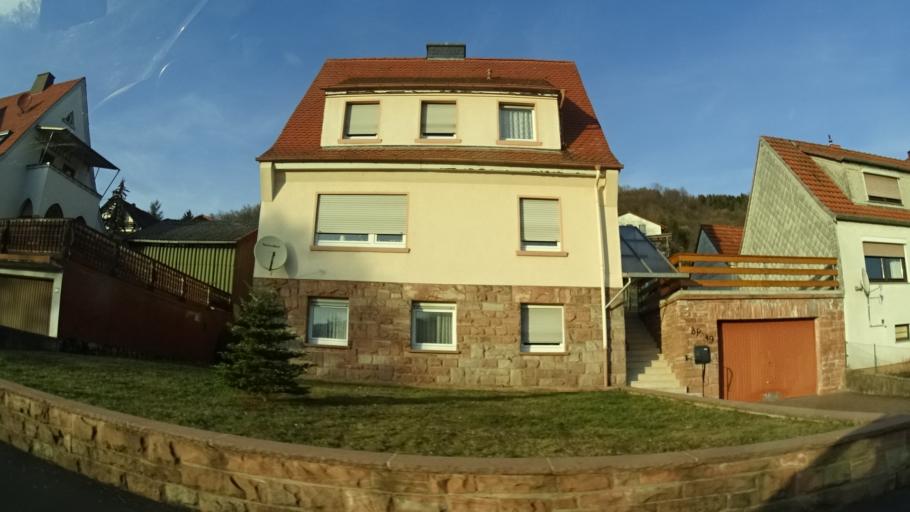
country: DE
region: Hesse
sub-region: Regierungsbezirk Darmstadt
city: Schluchtern
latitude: 50.3489
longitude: 9.5446
